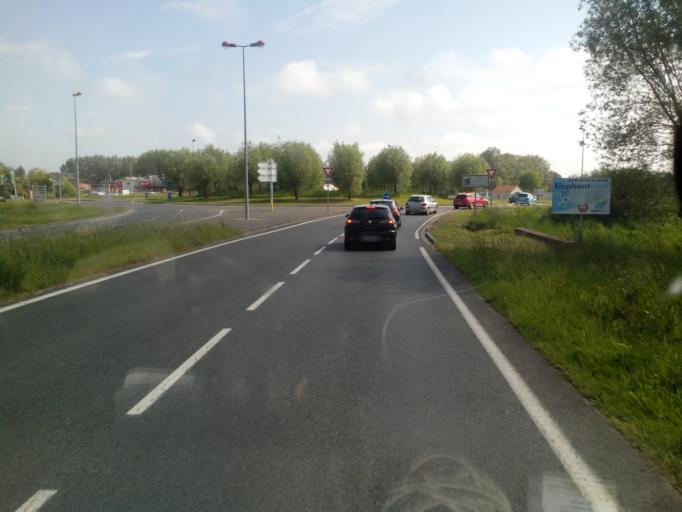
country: FR
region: Picardie
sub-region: Departement de la Somme
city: Rue
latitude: 50.2771
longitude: 1.6596
